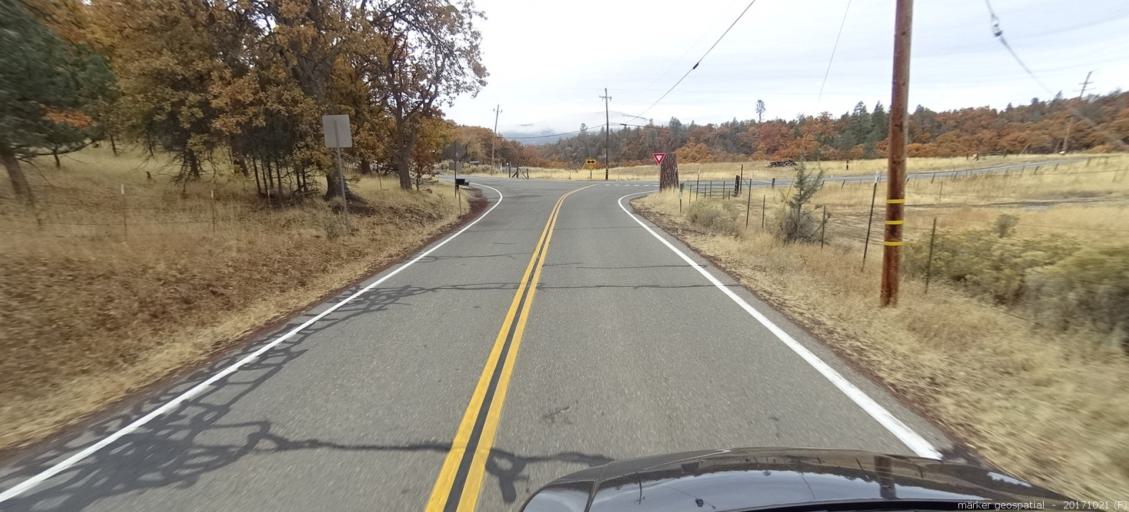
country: US
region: California
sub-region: Shasta County
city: Burney
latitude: 40.9999
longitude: -121.4329
